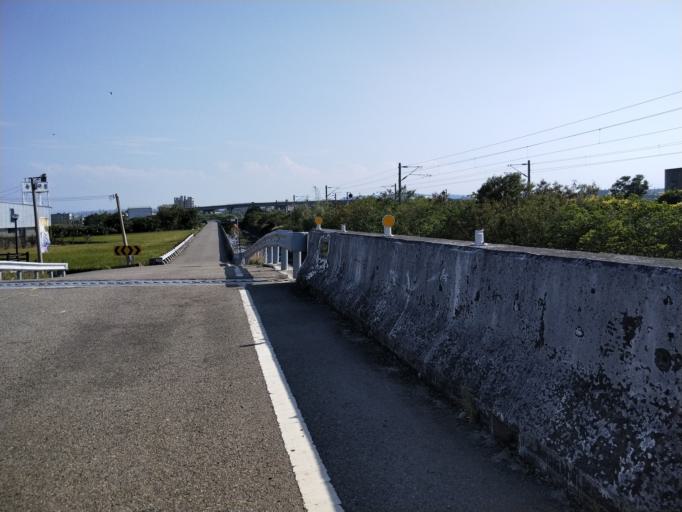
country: TW
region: Taiwan
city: Fengyuan
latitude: 24.4264
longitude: 120.6520
